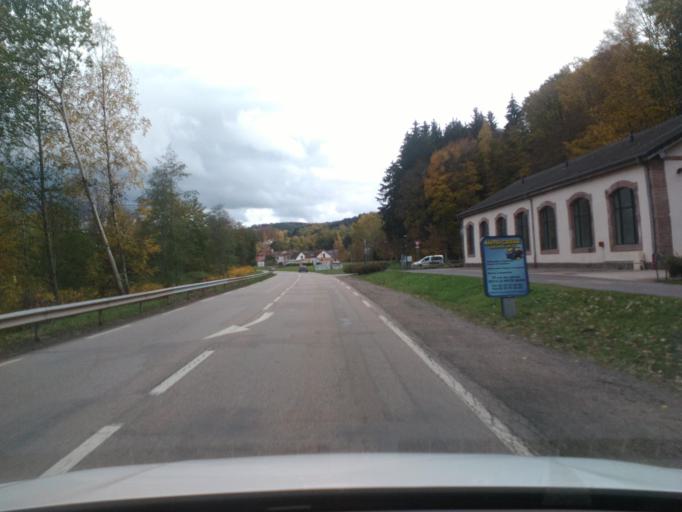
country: FR
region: Lorraine
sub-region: Departement des Vosges
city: Senones
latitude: 48.3913
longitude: 6.9663
